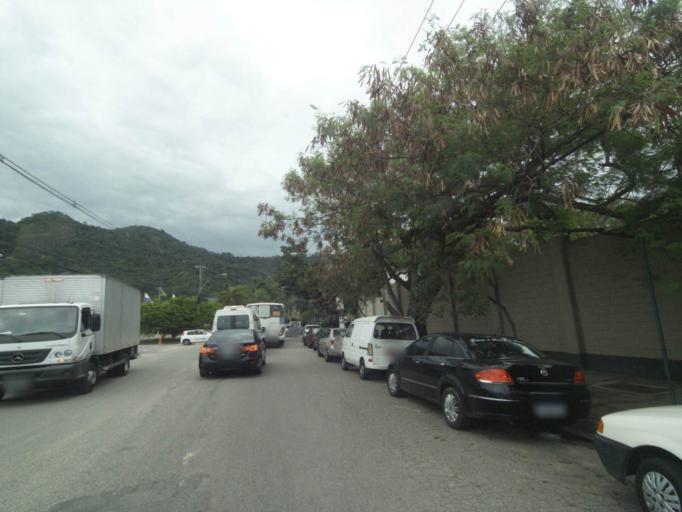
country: BR
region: Rio de Janeiro
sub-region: Nilopolis
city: Nilopolis
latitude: -22.9617
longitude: -43.4048
